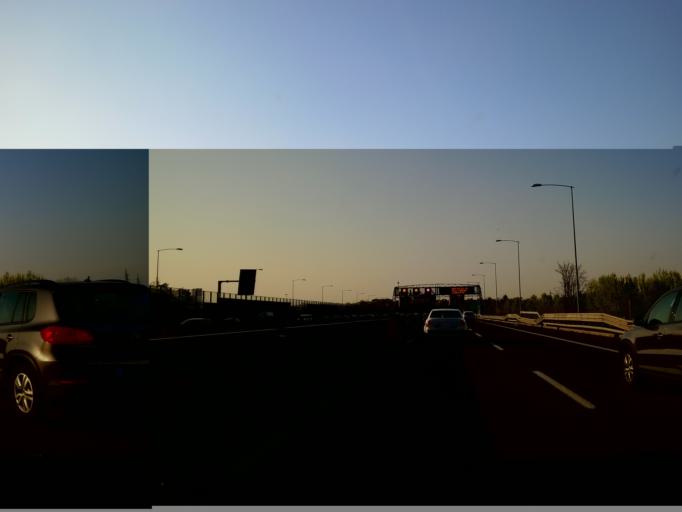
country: IT
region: Emilia-Romagna
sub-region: Provincia di Bologna
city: San Lazzaro
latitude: 44.5004
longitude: 11.3854
